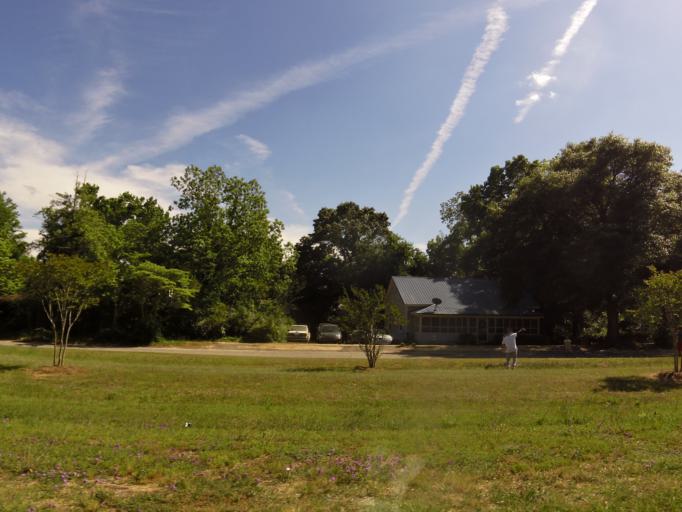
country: US
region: South Carolina
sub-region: Bamberg County
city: Denmark
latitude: 33.3267
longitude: -81.1451
